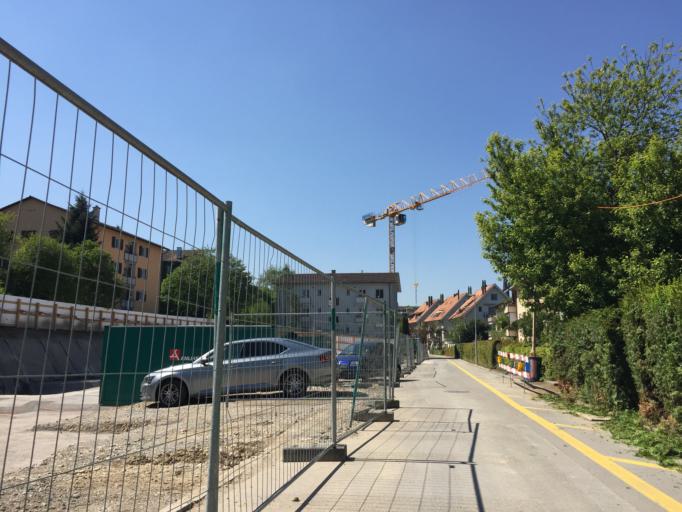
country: CH
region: Zurich
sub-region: Bezirk Zuerich
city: Zuerich (Kreis 11) / Oerlikon
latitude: 47.4037
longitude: 8.5532
